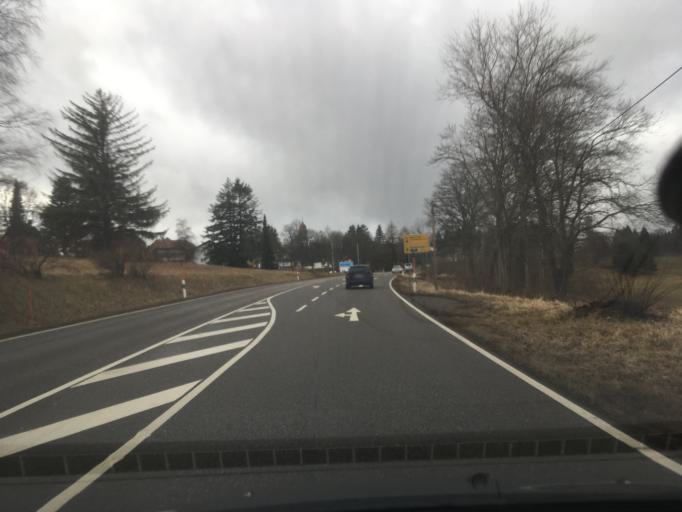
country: DE
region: Baden-Wuerttemberg
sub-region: Freiburg Region
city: Hochenschwand
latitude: 47.7376
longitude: 8.1715
